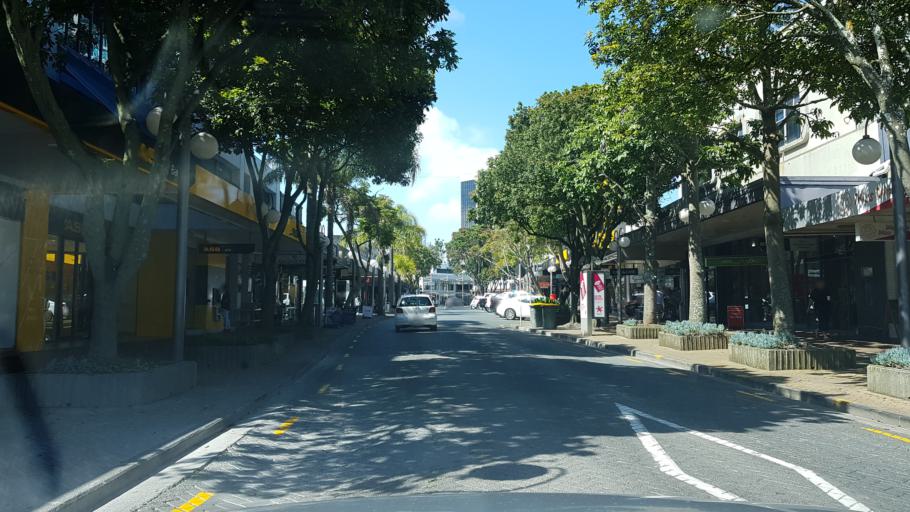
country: NZ
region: Auckland
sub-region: Auckland
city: North Shore
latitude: -36.7879
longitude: 174.7726
